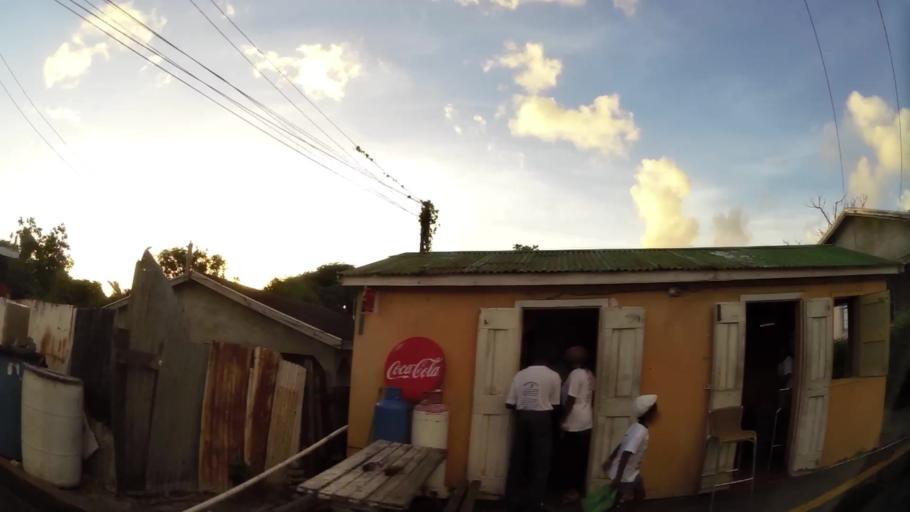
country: KN
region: Saint Anne Sandy Point
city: Sandy Point Town
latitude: 17.3888
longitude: -62.8519
